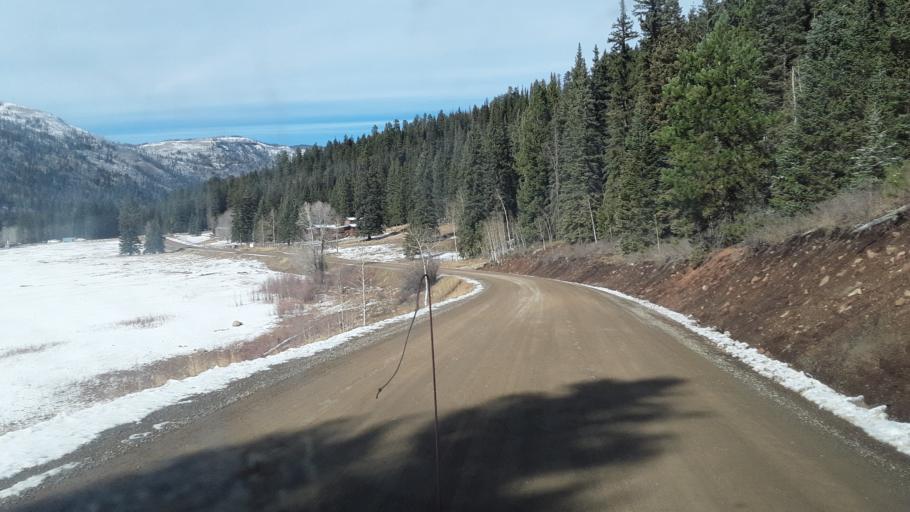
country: US
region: Colorado
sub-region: La Plata County
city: Bayfield
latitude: 37.4201
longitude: -107.6667
